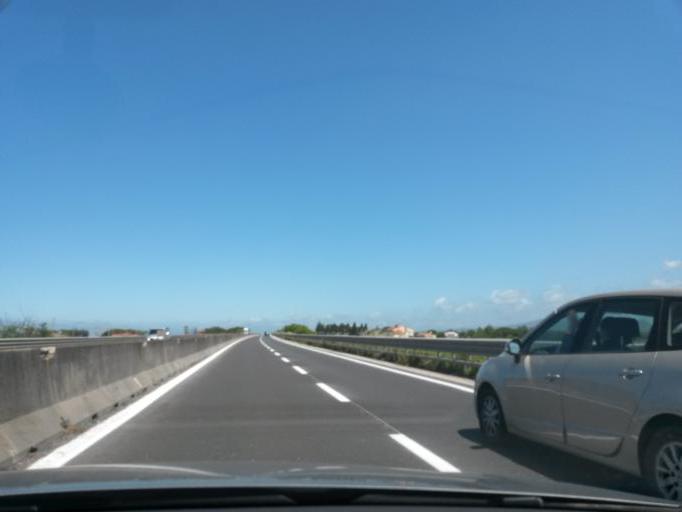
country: IT
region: Tuscany
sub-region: Provincia di Livorno
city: La California
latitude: 43.2624
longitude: 10.5434
